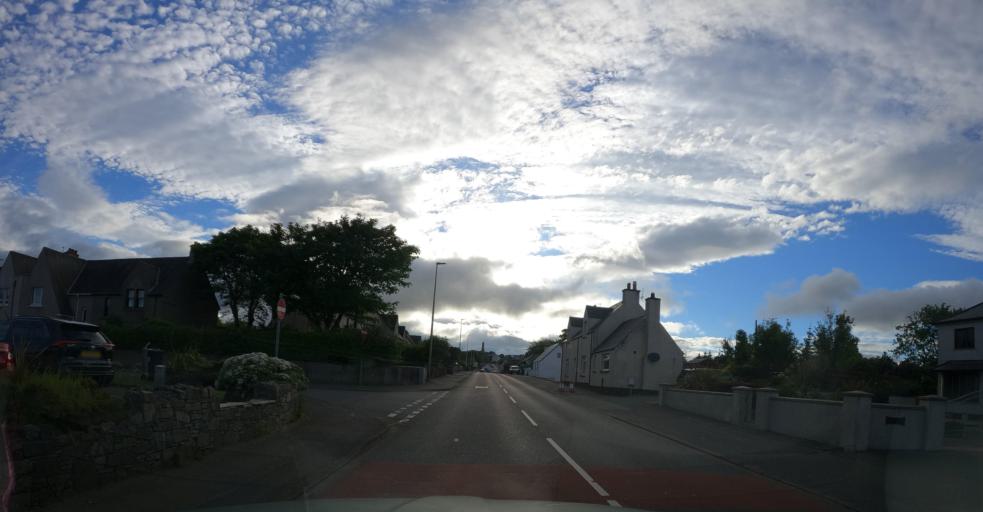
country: GB
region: Scotland
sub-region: Eilean Siar
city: Isle of Lewis
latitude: 58.2189
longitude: -6.3825
